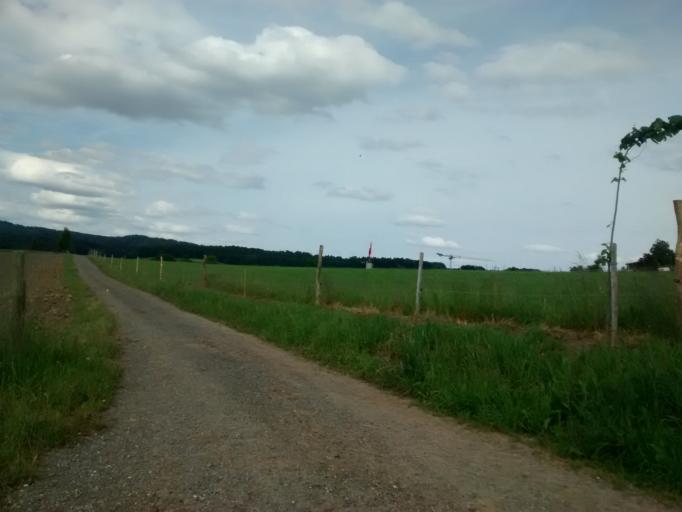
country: CH
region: Zurich
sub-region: Bezirk Affoltern
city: Bonstetten
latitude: 47.3116
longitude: 8.4590
